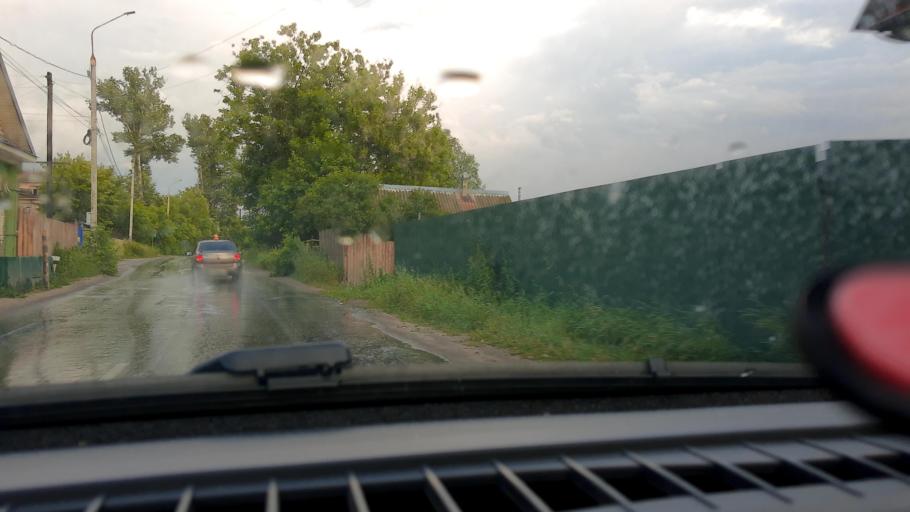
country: RU
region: Nizjnij Novgorod
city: Gorodets
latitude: 56.6620
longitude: 43.4595
